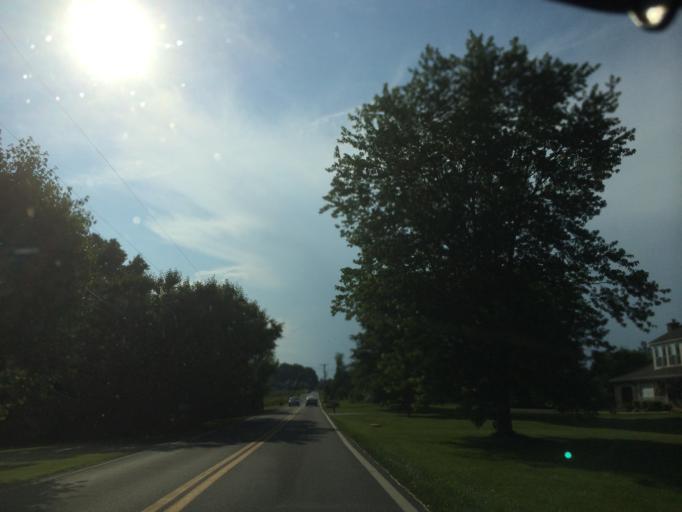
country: US
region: Maryland
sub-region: Carroll County
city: Sykesville
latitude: 39.4088
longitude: -77.0192
